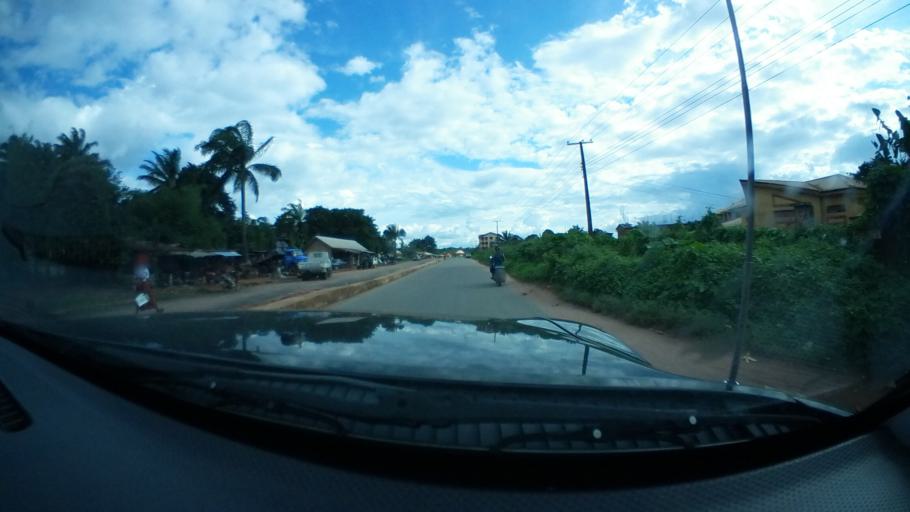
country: NG
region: Anambra
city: Uga
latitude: 5.9067
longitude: 7.1096
